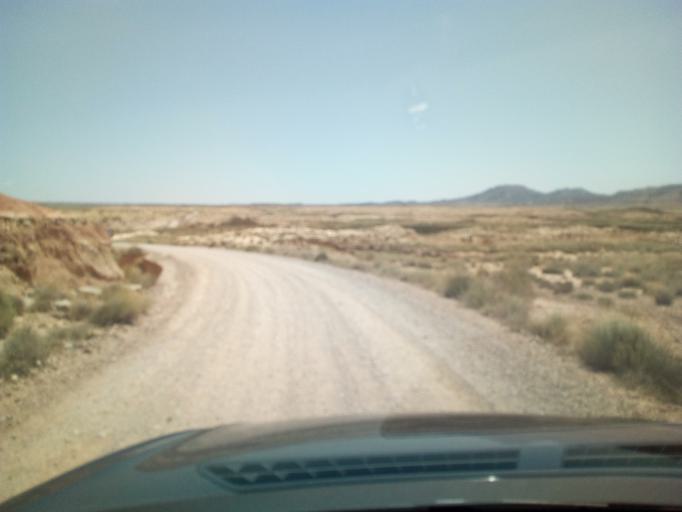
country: ES
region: Navarre
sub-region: Provincia de Navarra
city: Arguedas
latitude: 42.1829
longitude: -1.4784
